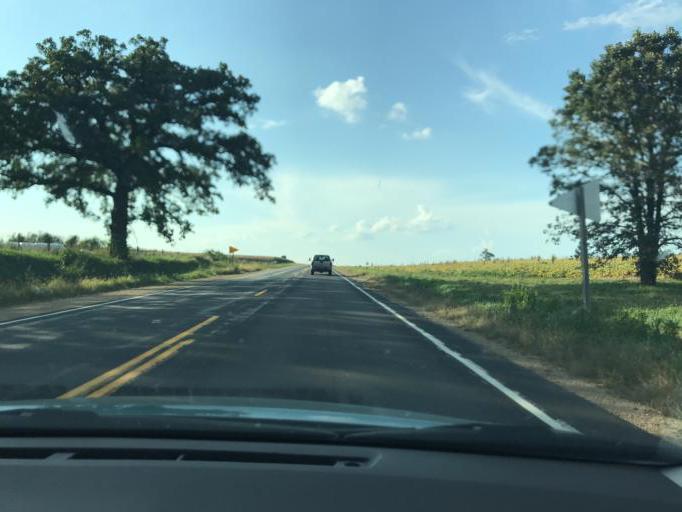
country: US
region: Wisconsin
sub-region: Grant County
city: Platteville
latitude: 42.7071
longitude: -90.4462
